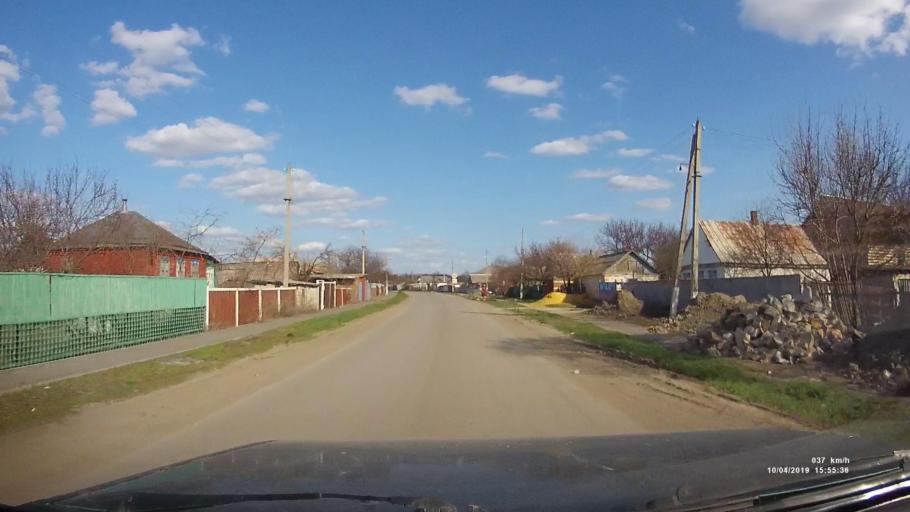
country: RU
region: Rostov
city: Masalovka
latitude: 48.4122
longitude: 40.2661
